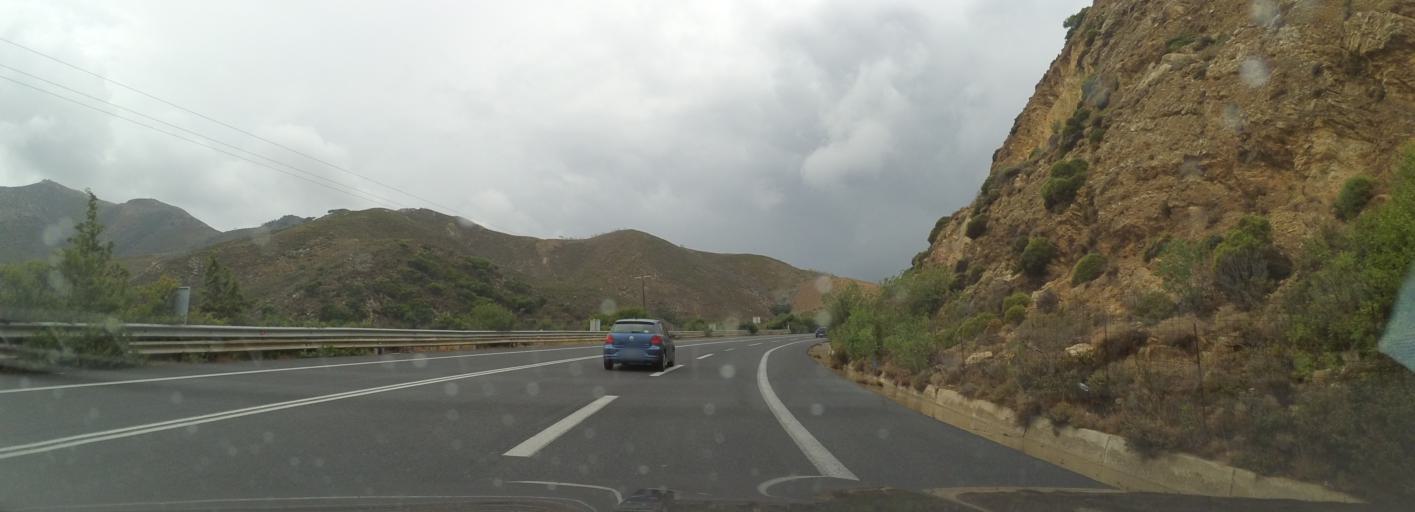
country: GR
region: Crete
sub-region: Nomos Rethymnis
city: Anogeia
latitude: 35.3879
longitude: 24.9373
